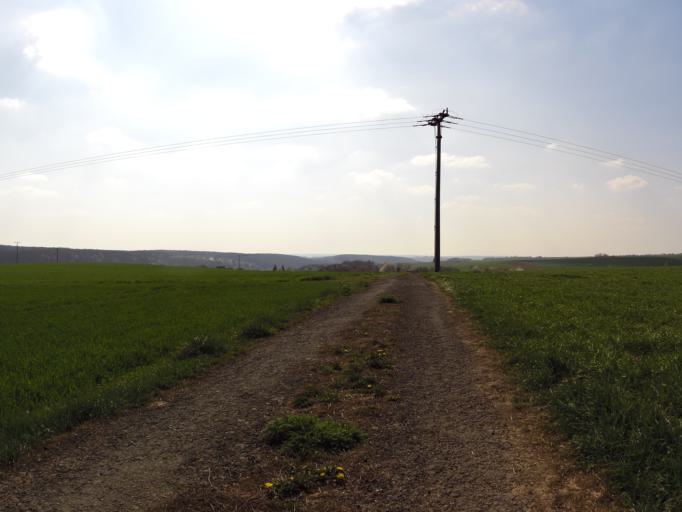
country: DE
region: Bavaria
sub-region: Regierungsbezirk Unterfranken
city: Theilheim
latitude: 49.7606
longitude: 10.0443
